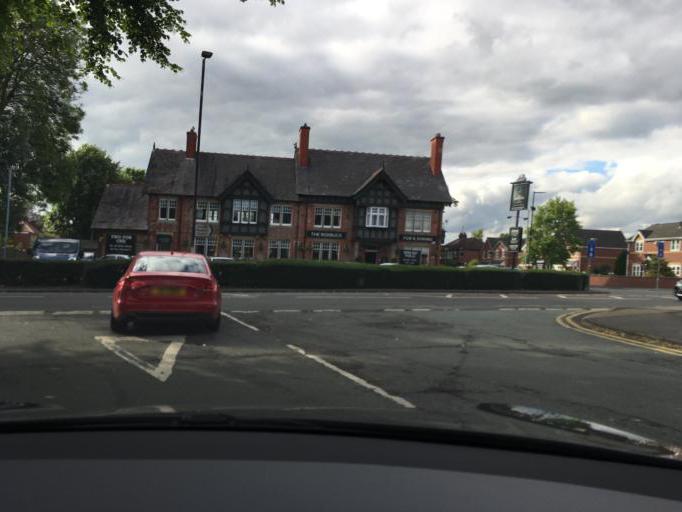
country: GB
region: England
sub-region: Trafford
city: Urmston
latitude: 53.4433
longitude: -2.3661
